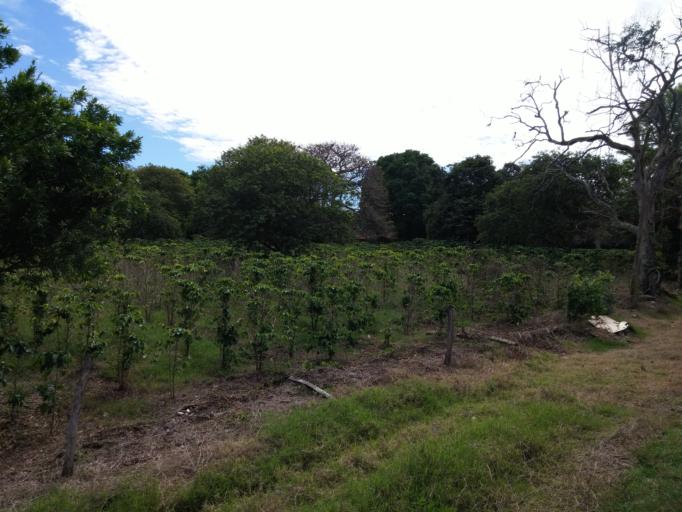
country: CR
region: Heredia
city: Mercedes
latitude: 9.9991
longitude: -84.1389
